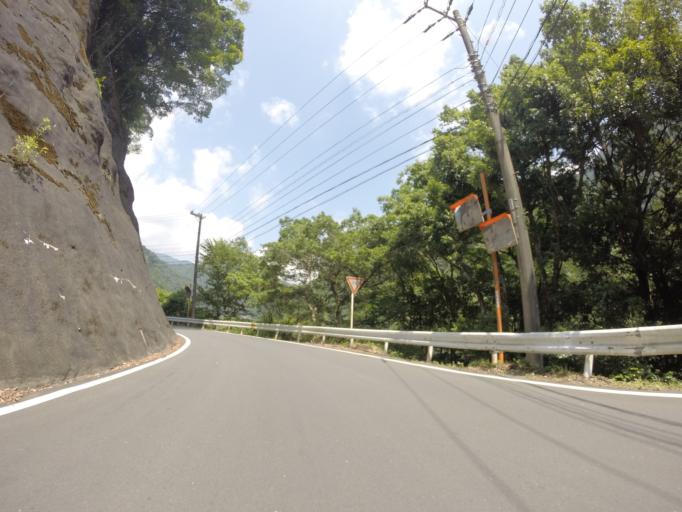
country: JP
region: Shizuoka
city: Shizuoka-shi
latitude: 35.2303
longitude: 138.3473
